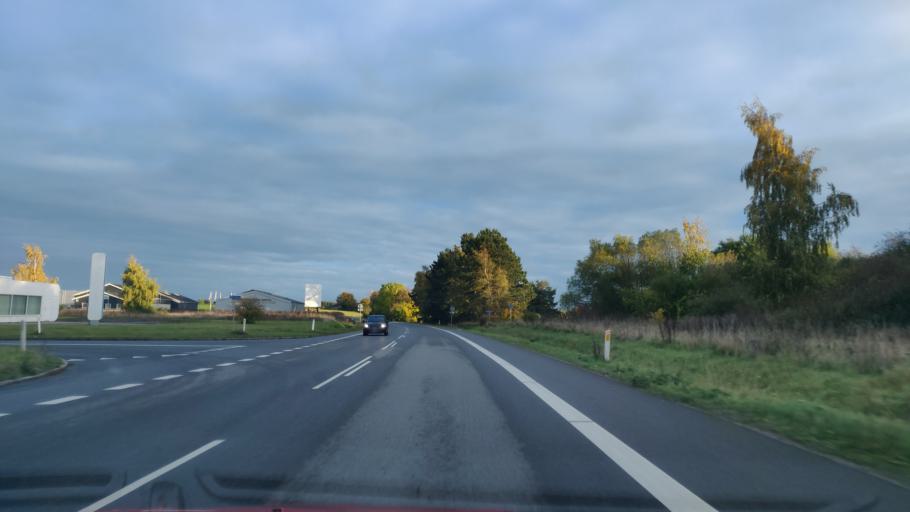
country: DK
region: Zealand
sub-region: Holbaek Kommune
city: Holbaek
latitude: 55.6867
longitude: 11.6996
